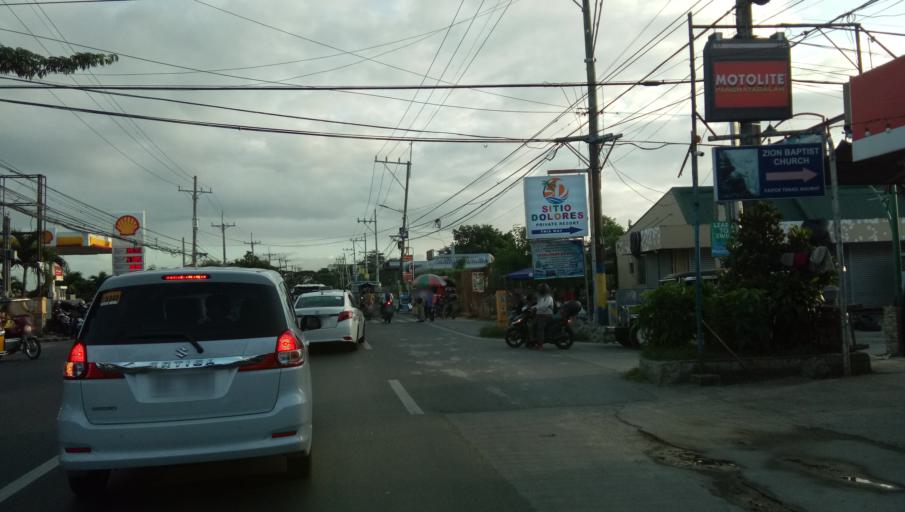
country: PH
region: Calabarzon
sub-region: Province of Cavite
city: Imus
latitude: 14.3802
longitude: 120.9788
